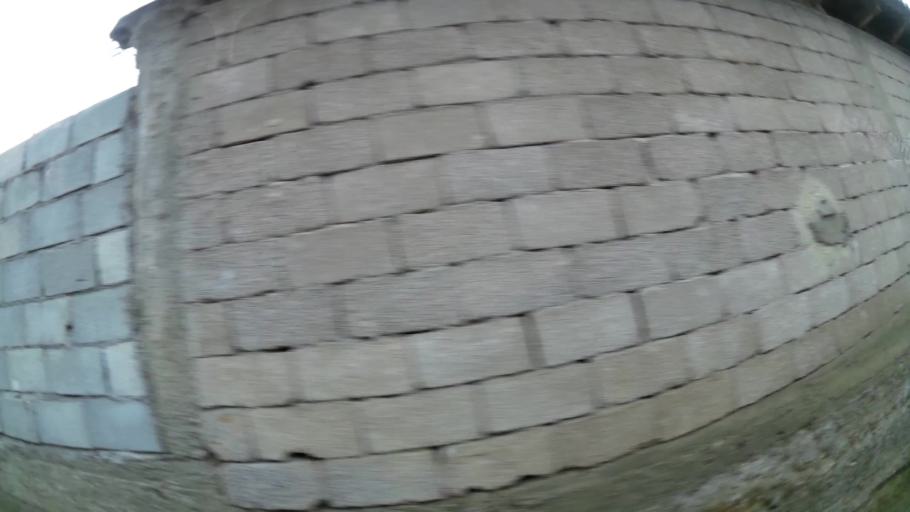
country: MK
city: Kondovo
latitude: 42.0129
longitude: 21.3154
